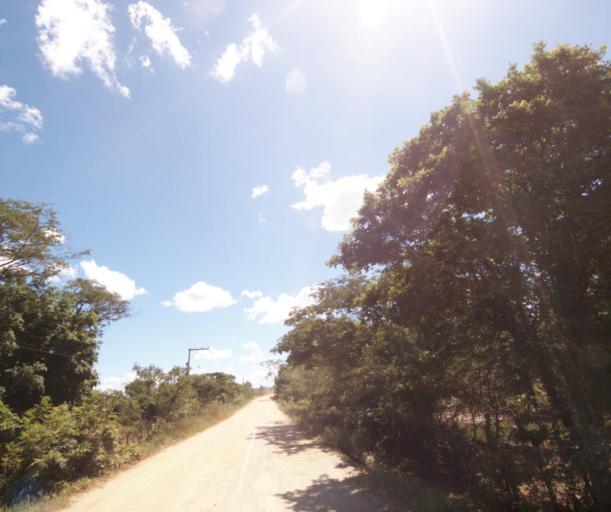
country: BR
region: Bahia
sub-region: Carinhanha
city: Carinhanha
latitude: -14.2155
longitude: -44.2851
